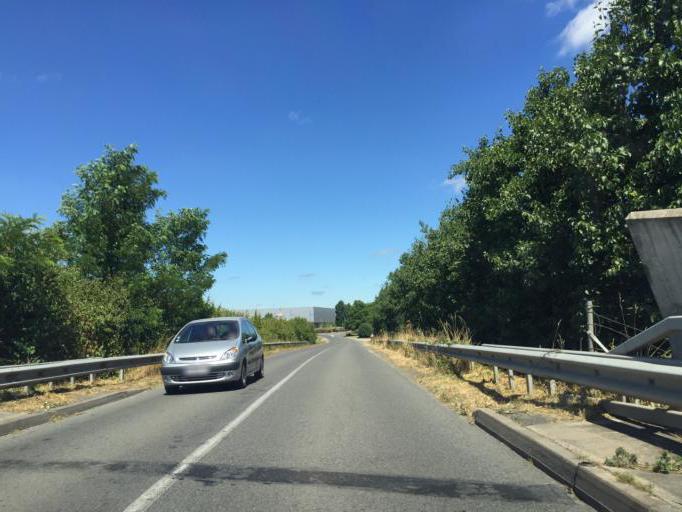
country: FR
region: Auvergne
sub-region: Departement de l'Allier
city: Moulins
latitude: 46.5912
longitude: 3.3324
